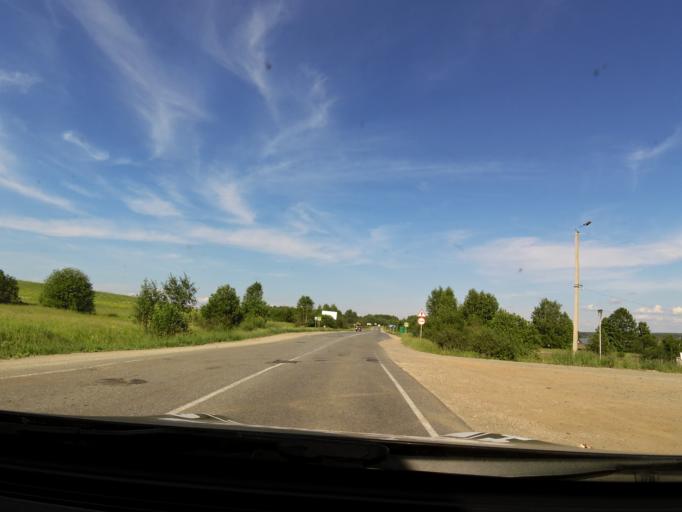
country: RU
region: Kirov
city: Belaya Kholunitsa
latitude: 58.8926
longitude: 50.8818
